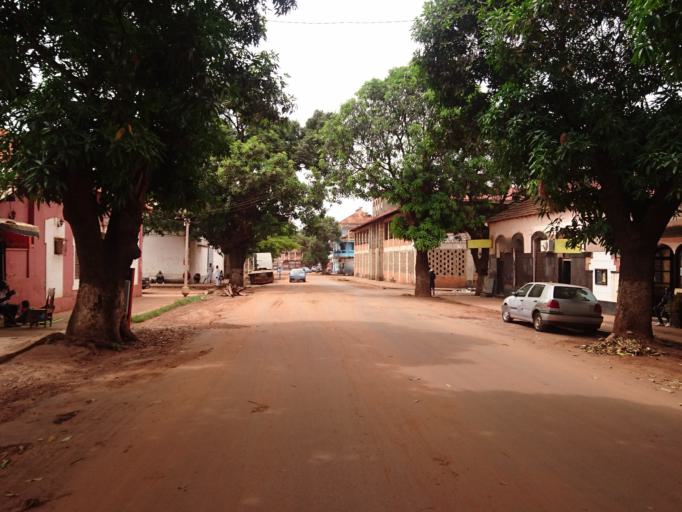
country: GW
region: Bissau
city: Bissau
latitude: 11.8610
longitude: -15.5809
